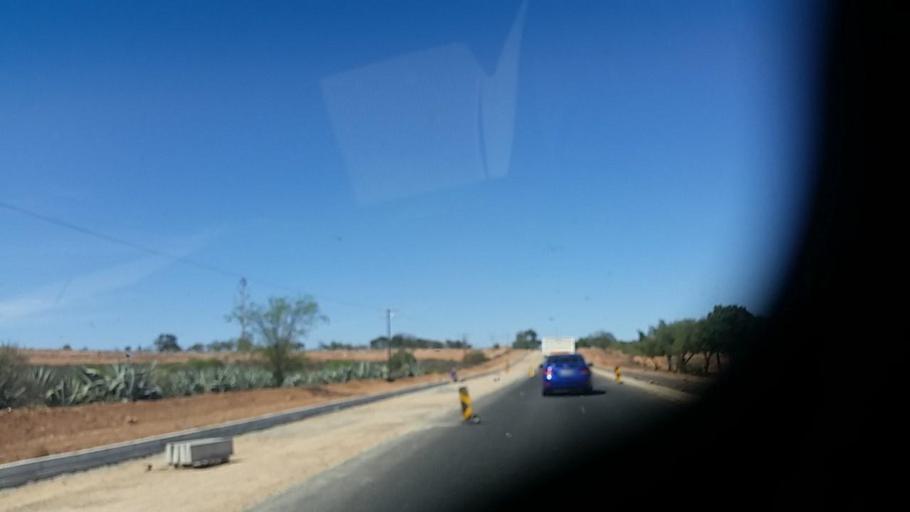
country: ZA
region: Western Cape
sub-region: Eden District Municipality
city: Oudtshoorn
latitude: -33.5937
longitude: 22.2262
